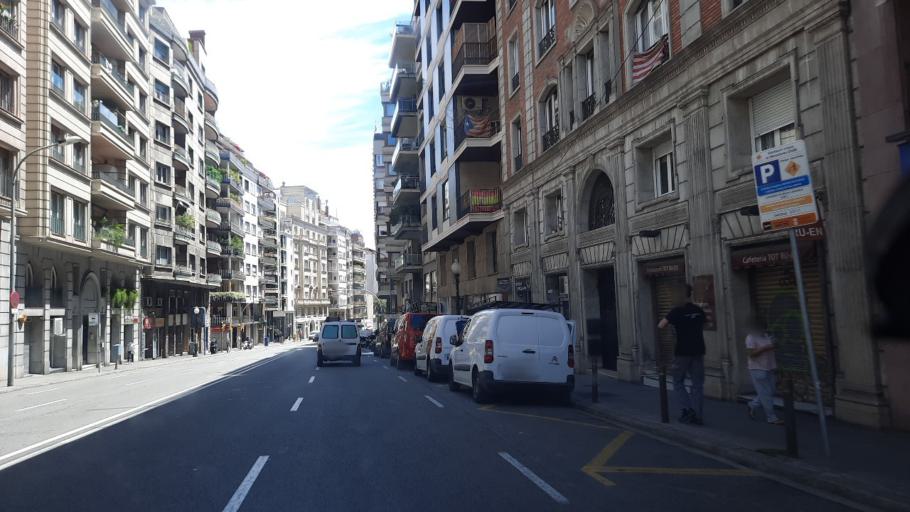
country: ES
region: Catalonia
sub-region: Provincia de Barcelona
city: Sarria-Sant Gervasi
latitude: 41.4031
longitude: 2.1434
